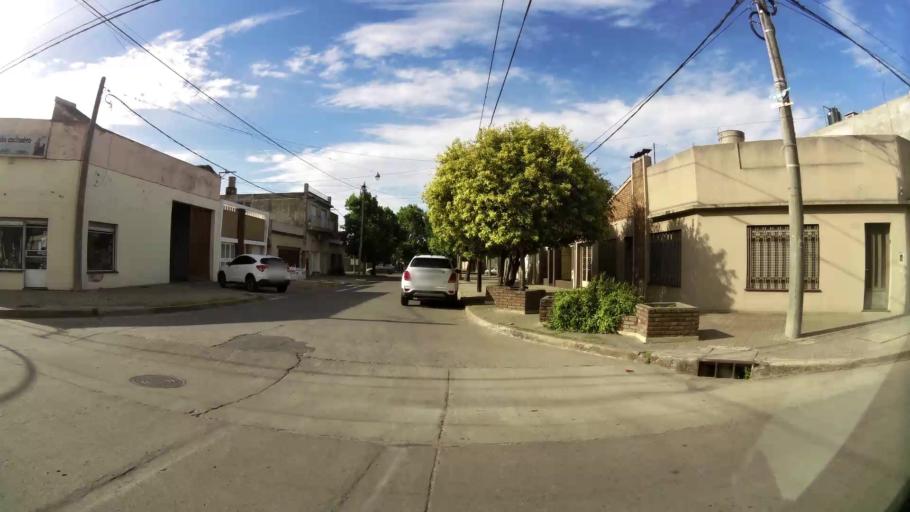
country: AR
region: Santa Fe
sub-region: Departamento de Rosario
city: Rosario
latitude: -32.9269
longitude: -60.6885
